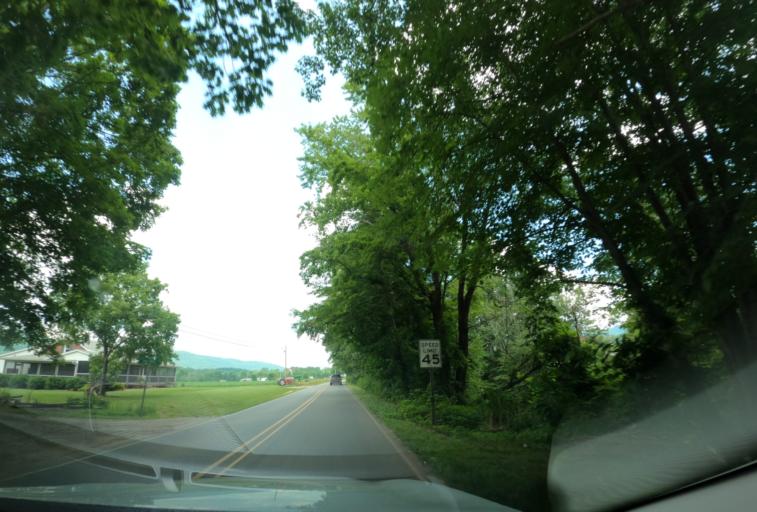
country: US
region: North Carolina
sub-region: Haywood County
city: Clyde
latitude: 35.4644
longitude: -82.8996
